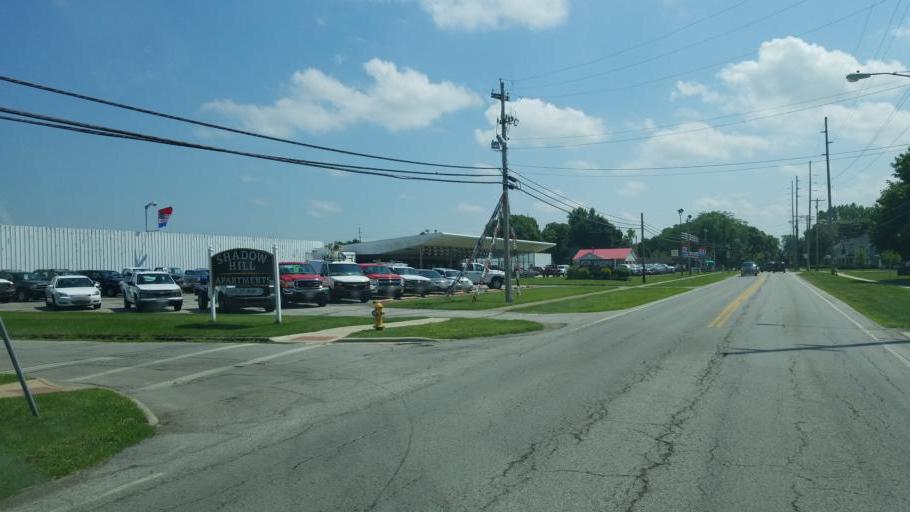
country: US
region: Ohio
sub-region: Huron County
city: Bellevue
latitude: 41.2862
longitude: -82.8370
